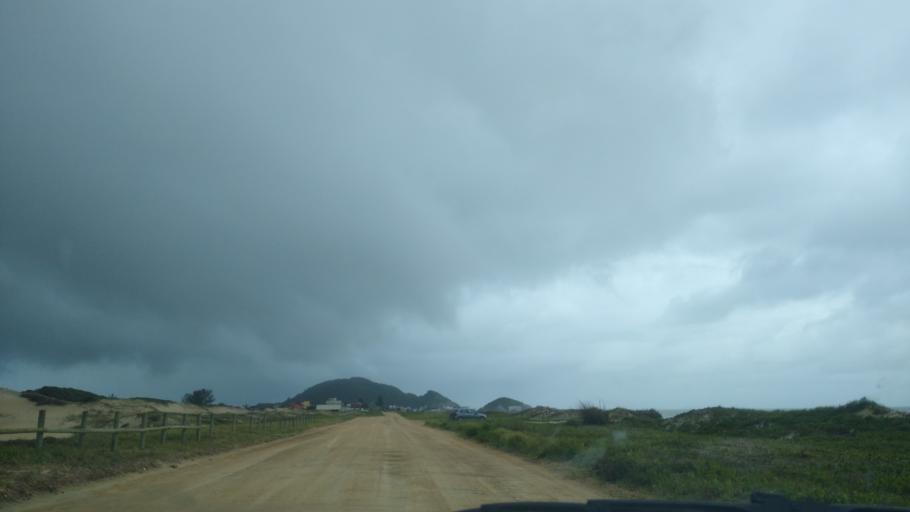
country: BR
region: Santa Catarina
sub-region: Sao Francisco Do Sul
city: Sao Francisco do Sul
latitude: -26.2442
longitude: -48.5092
